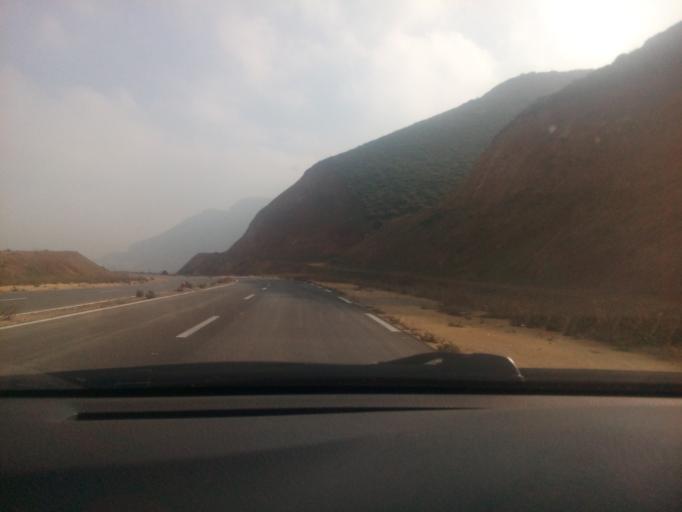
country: DZ
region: Oran
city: Mers el Kebir
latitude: 35.7154
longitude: -0.7062
